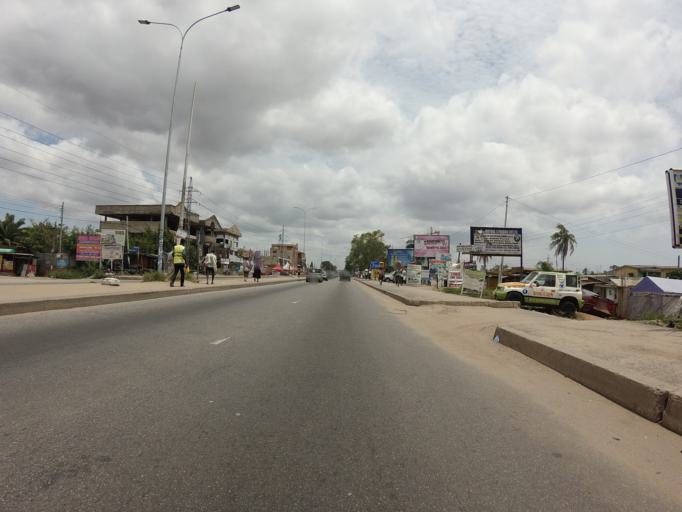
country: GH
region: Greater Accra
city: Gbawe
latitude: 5.5751
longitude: -0.2763
